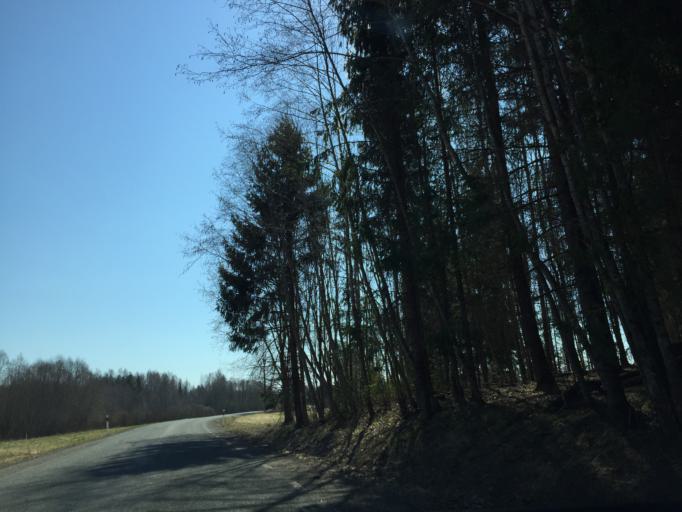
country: EE
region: Tartu
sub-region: Alatskivi vald
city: Kallaste
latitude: 58.5805
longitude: 26.9079
